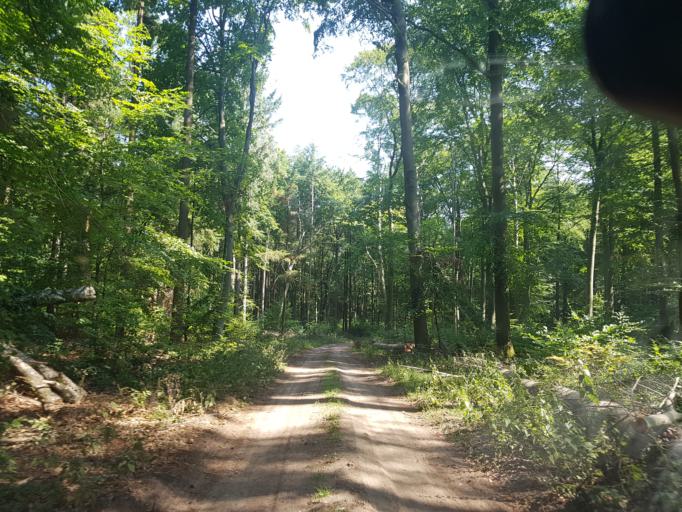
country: DE
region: Brandenburg
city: Gorzke
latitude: 52.0736
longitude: 12.3606
